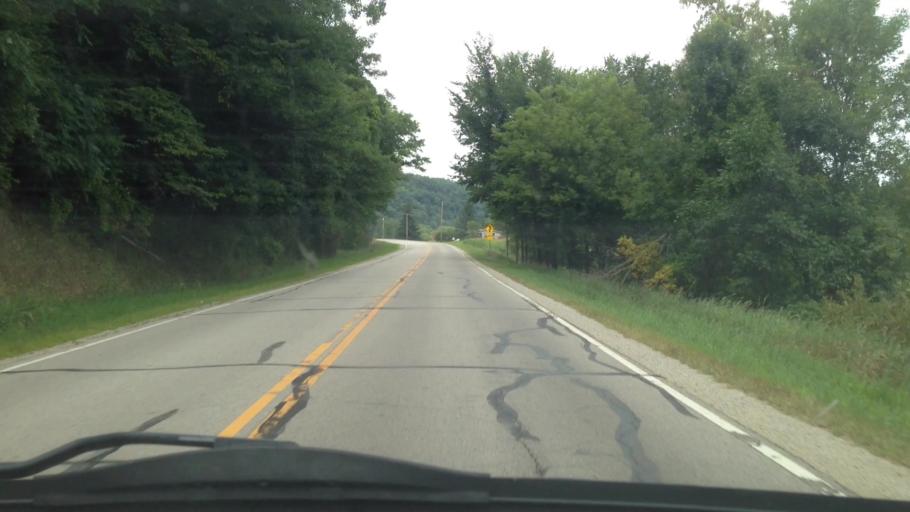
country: US
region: Minnesota
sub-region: Fillmore County
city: Preston
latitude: 43.7244
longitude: -91.9629
